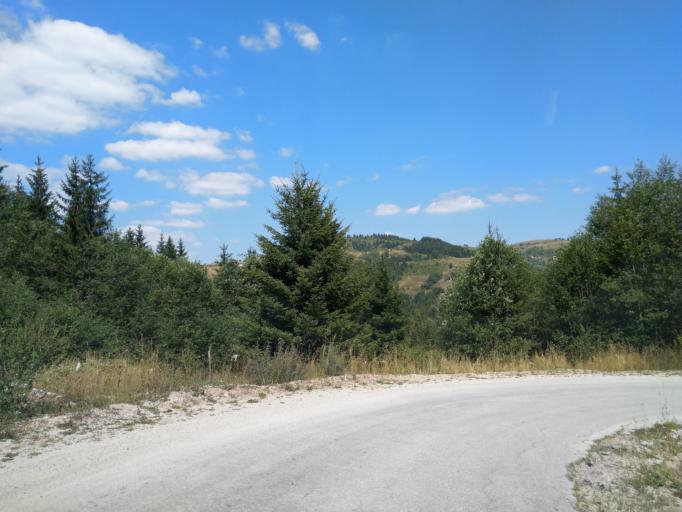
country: RS
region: Central Serbia
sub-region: Zlatiborski Okrug
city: Nova Varos
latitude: 43.4796
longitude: 19.9702
